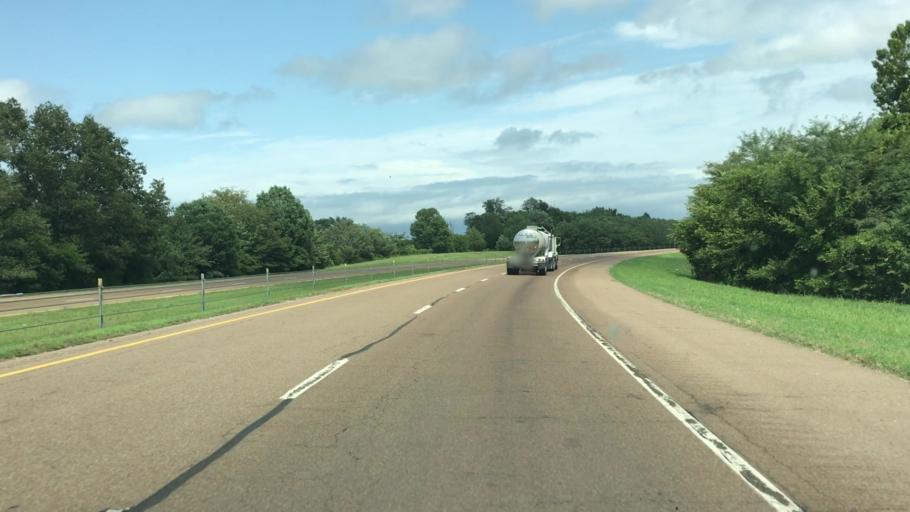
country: US
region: Tennessee
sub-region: Obion County
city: Union City
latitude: 36.4578
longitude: -88.9953
